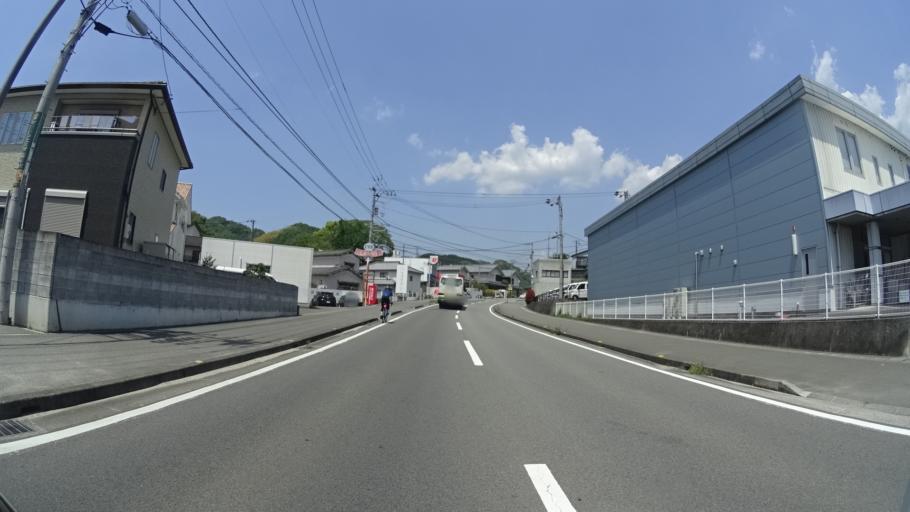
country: JP
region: Ehime
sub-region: Shikoku-chuo Shi
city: Matsuyama
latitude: 33.8549
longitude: 132.8101
